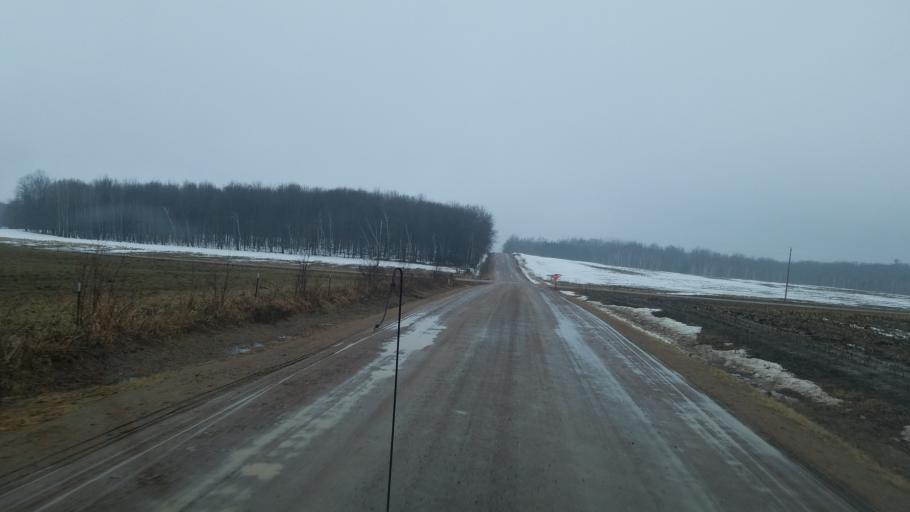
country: US
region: Wisconsin
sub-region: Clark County
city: Loyal
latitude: 44.6128
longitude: -90.3970
